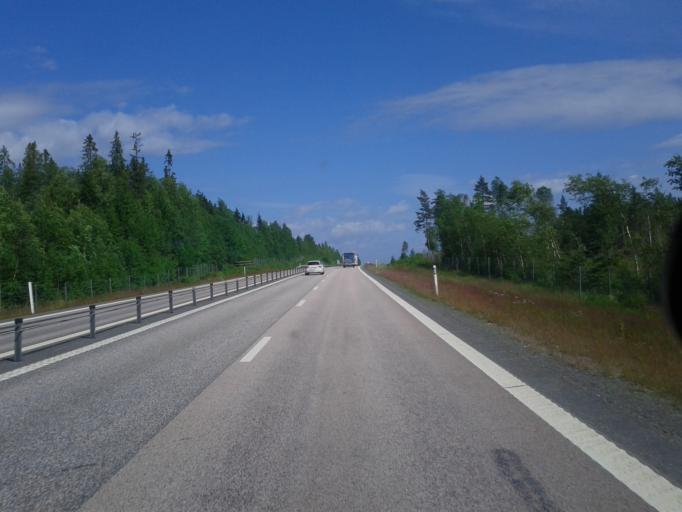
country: SE
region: Vaesternorrland
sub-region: OErnskoeldsviks Kommun
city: Husum
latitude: 63.4470
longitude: 19.2213
